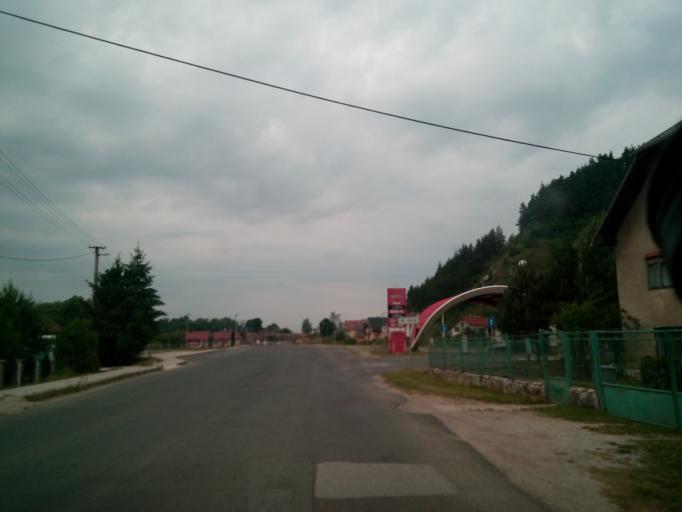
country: SK
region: Kosicky
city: Spisska Nova Ves
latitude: 48.9123
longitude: 20.6348
